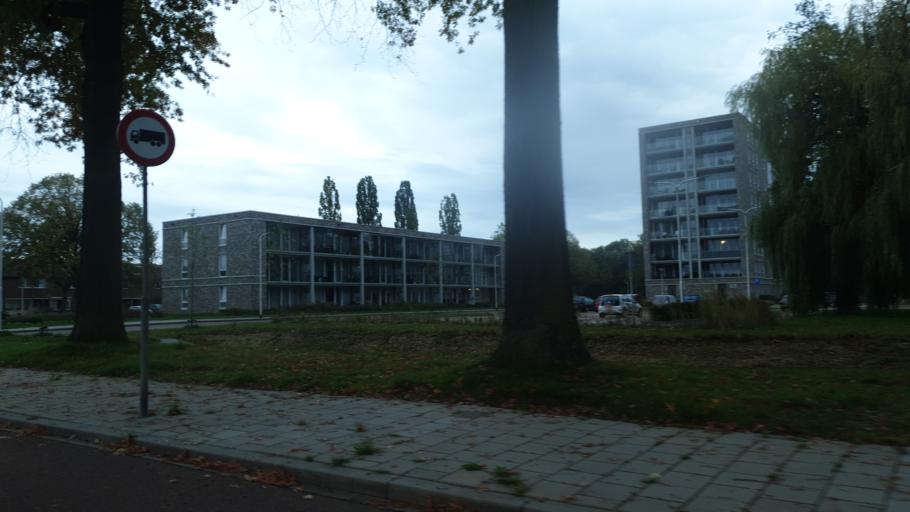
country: NL
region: Gelderland
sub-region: Gemeente Nijmegen
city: Lindenholt
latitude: 51.8061
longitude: 5.8119
